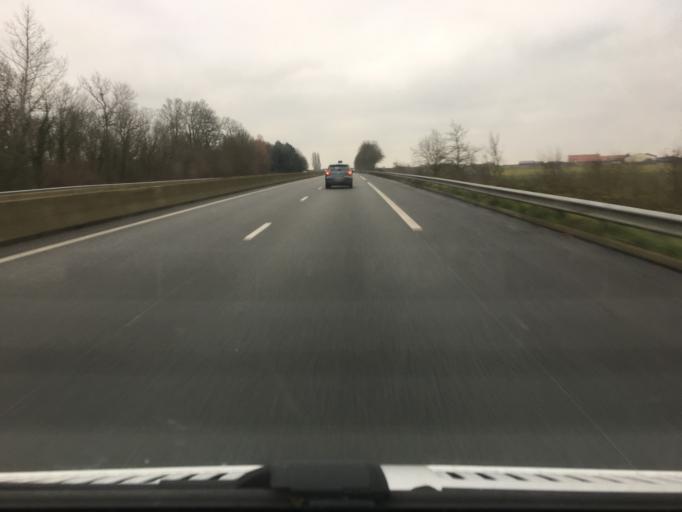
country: FR
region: Nord-Pas-de-Calais
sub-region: Departement du Nord
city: Godewaersvelde
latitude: 50.7842
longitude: 2.6241
